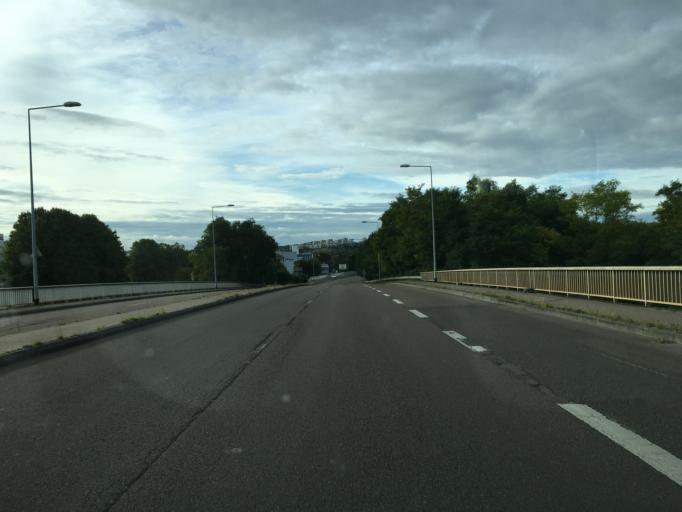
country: FR
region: Bourgogne
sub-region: Departement de la Cote-d'Or
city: Dijon
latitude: 47.3173
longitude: 5.0119
